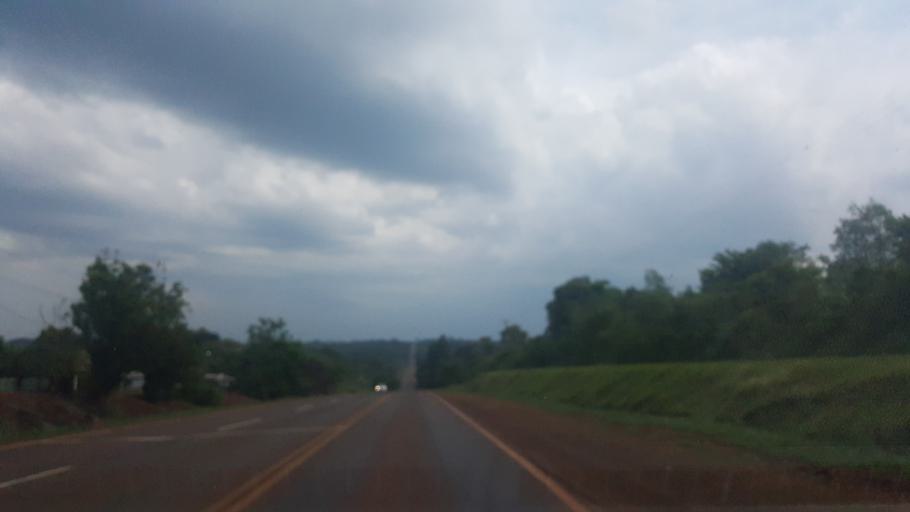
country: AR
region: Misiones
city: Jardin America
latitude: -27.0850
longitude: -55.2883
